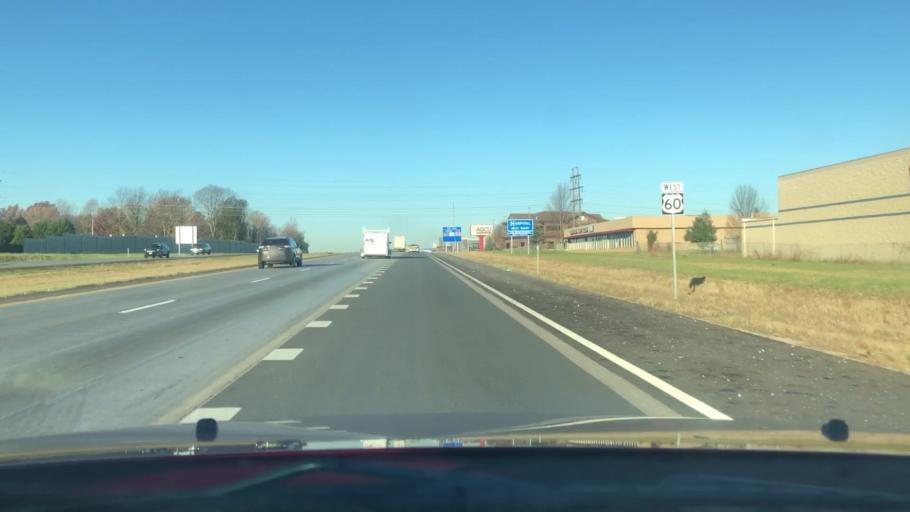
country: US
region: Missouri
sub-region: Greene County
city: Springfield
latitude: 37.1410
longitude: -93.2612
